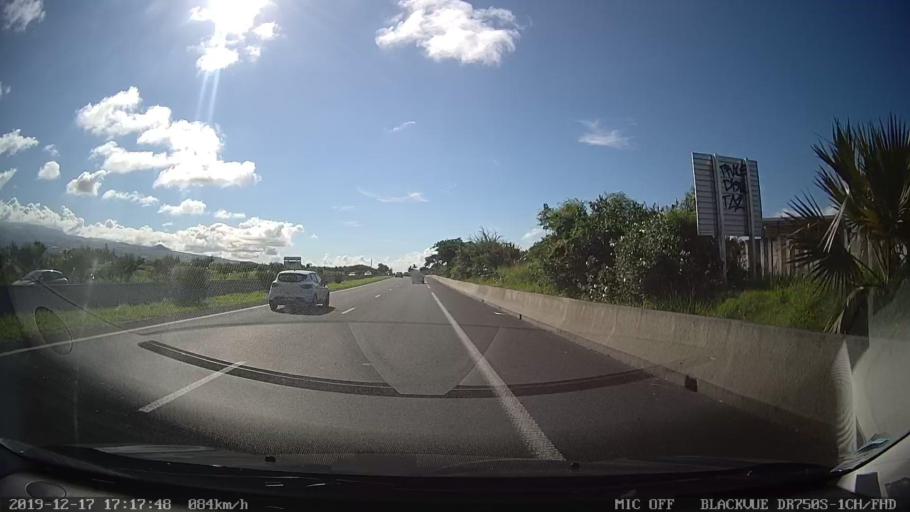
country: RE
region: Reunion
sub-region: Reunion
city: Saint-Louis
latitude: -21.3104
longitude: 55.4335
